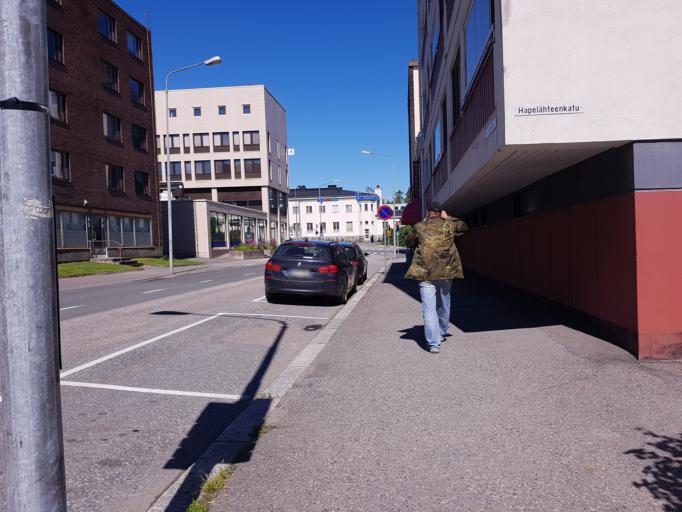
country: FI
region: Northern Savo
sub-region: Kuopio
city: Kuopio
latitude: 62.8960
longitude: 27.6815
